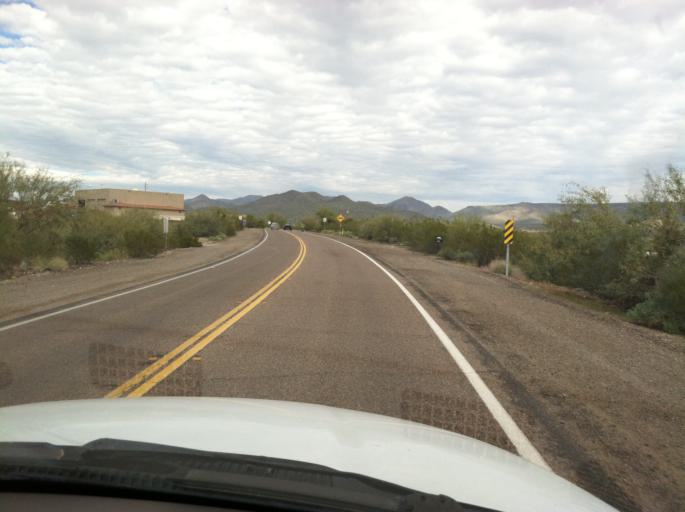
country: US
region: Arizona
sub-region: Maricopa County
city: New River
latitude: 33.9188
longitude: -112.1294
